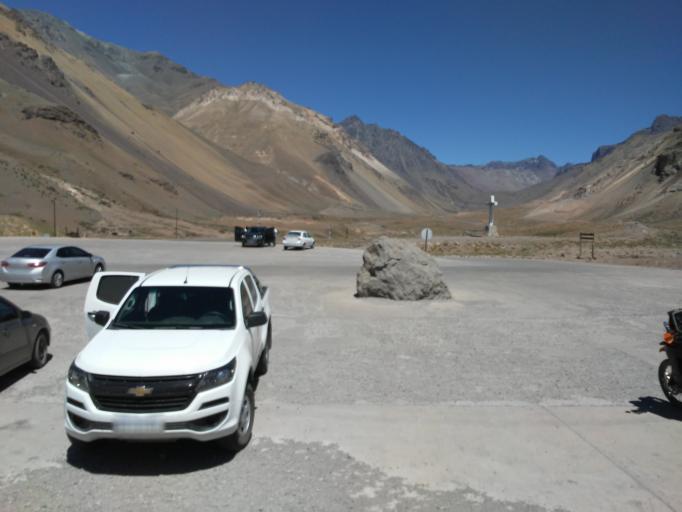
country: CL
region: Valparaiso
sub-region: Provincia de Los Andes
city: Los Andes
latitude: -32.8234
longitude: -69.9421
